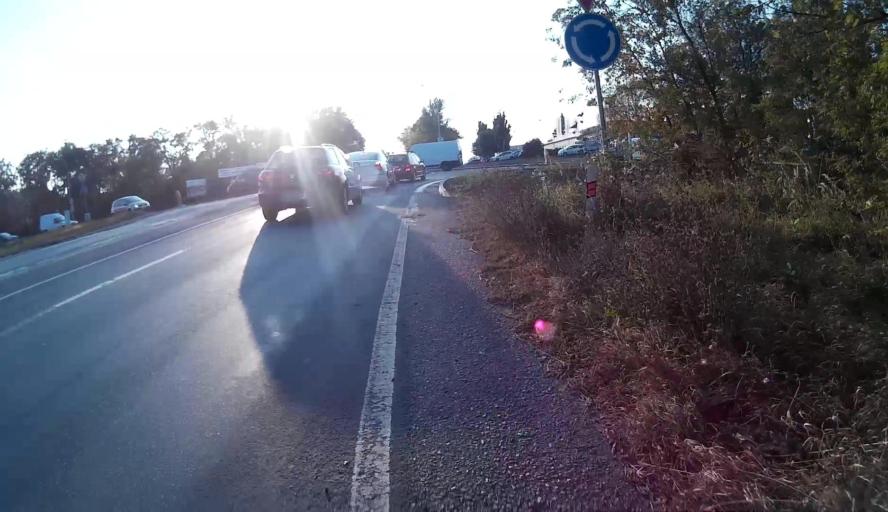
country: CZ
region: South Moravian
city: Podoli
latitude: 49.1824
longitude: 16.6925
